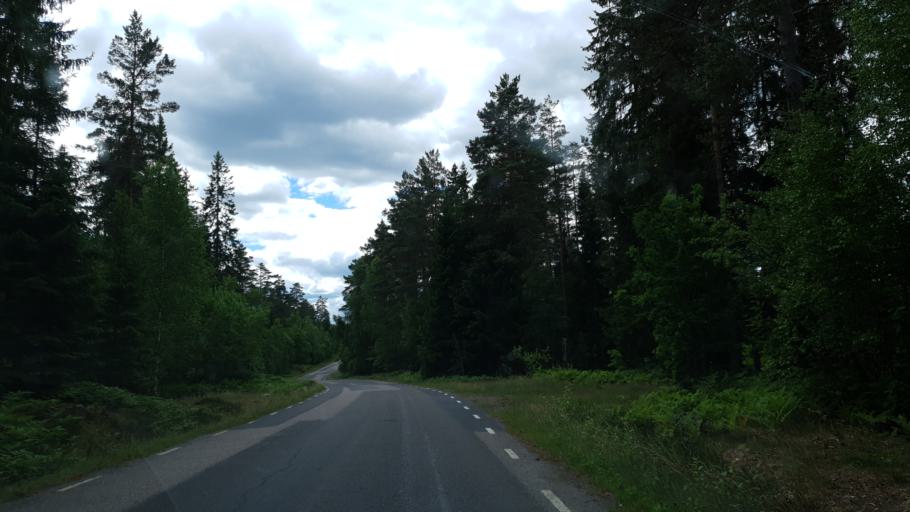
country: SE
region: Kalmar
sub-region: Hultsfreds Kommun
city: Virserum
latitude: 57.0640
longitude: 15.5967
